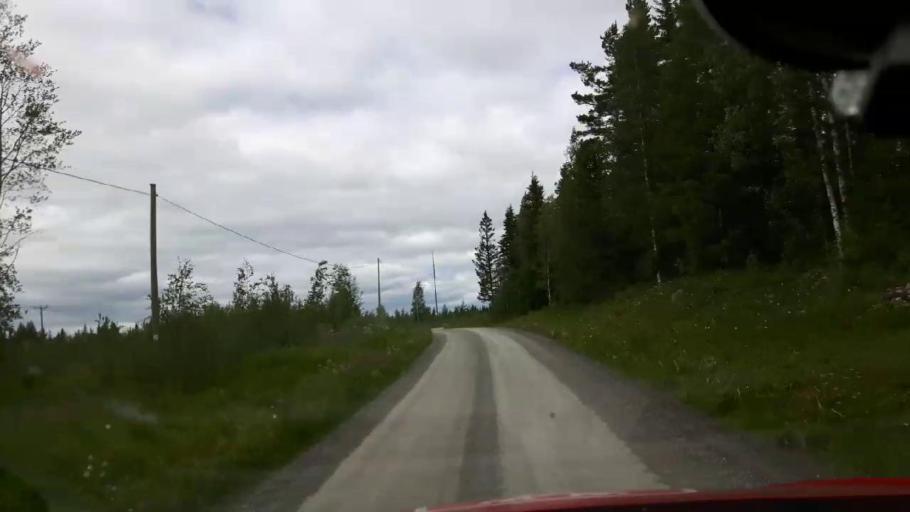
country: SE
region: Jaemtland
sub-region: OEstersunds Kommun
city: Brunflo
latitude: 63.0561
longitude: 14.9131
